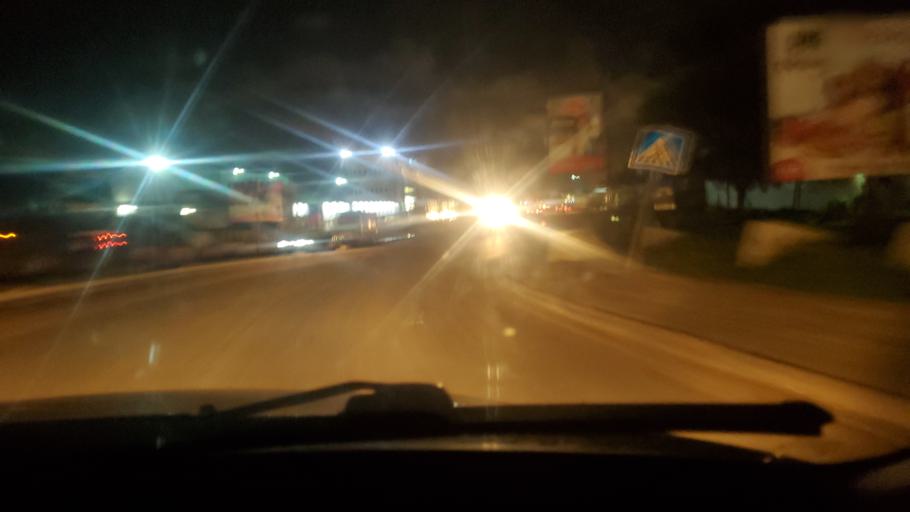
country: SN
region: Dakar
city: Pikine
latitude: 14.7429
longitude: -17.3946
